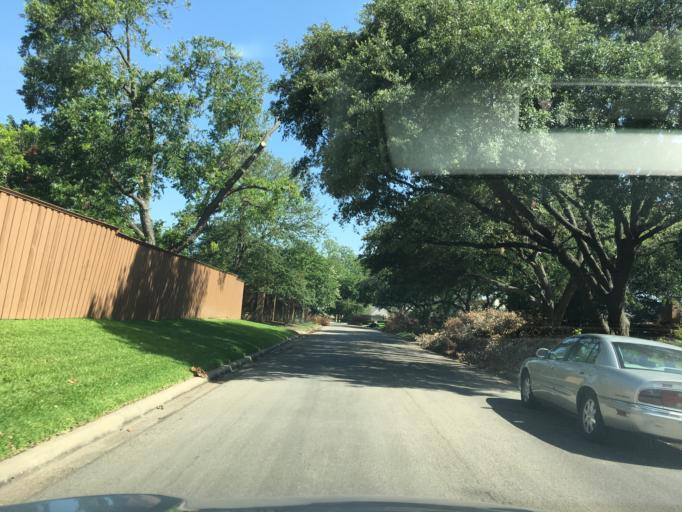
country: US
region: Texas
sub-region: Dallas County
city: University Park
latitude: 32.9040
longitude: -96.7726
